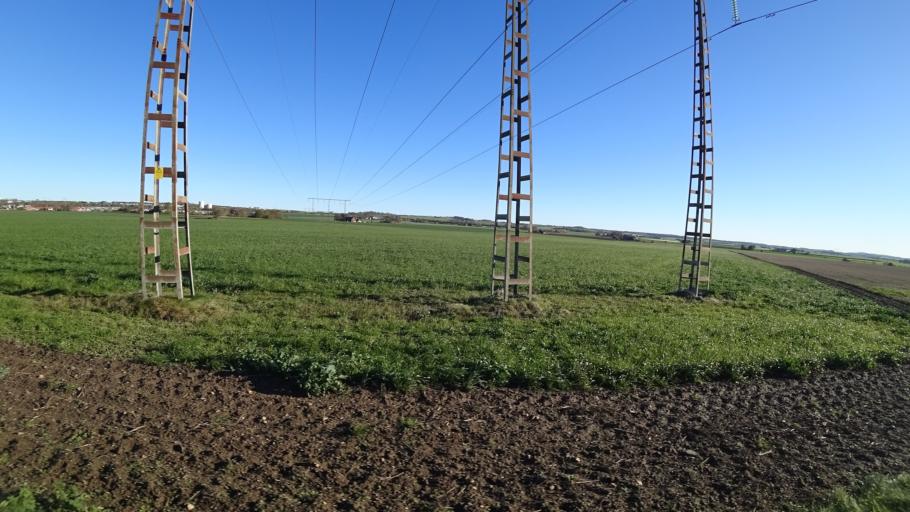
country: SE
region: Skane
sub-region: Staffanstorps Kommun
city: Staffanstorp
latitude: 55.6759
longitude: 13.2309
